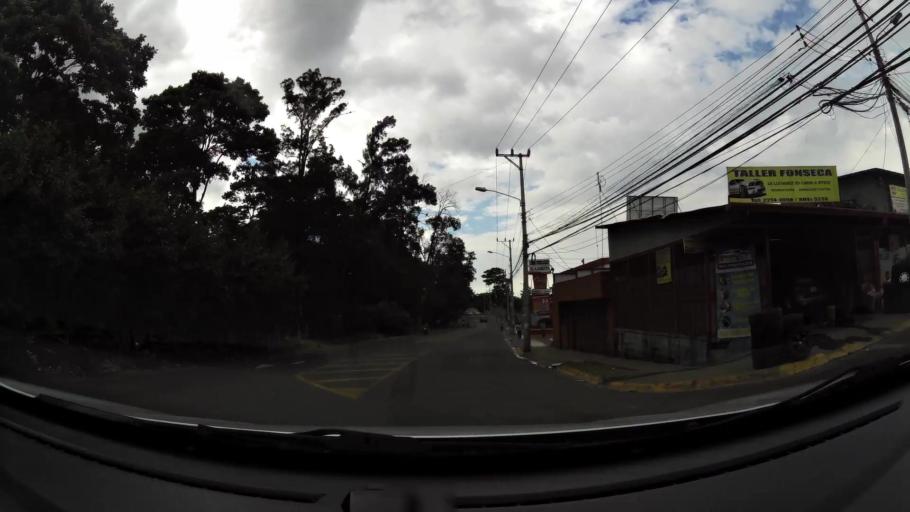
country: CR
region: San Jose
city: San Felipe
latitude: 9.9141
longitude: -84.1137
